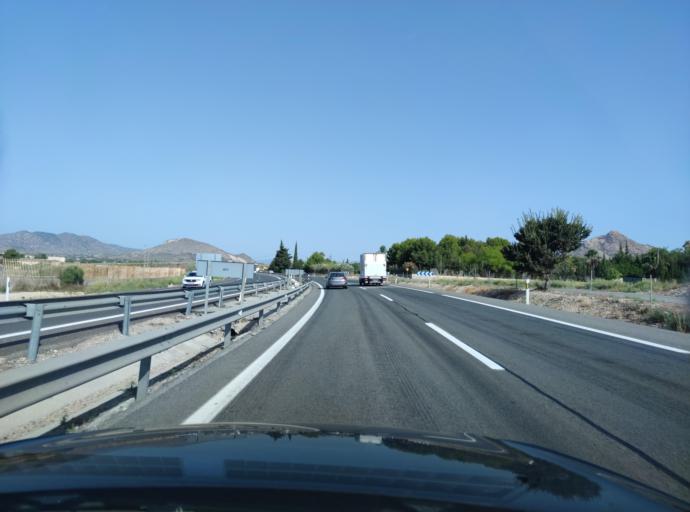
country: ES
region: Valencia
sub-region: Provincia de Alicante
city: Novelda
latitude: 38.3969
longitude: -0.7522
